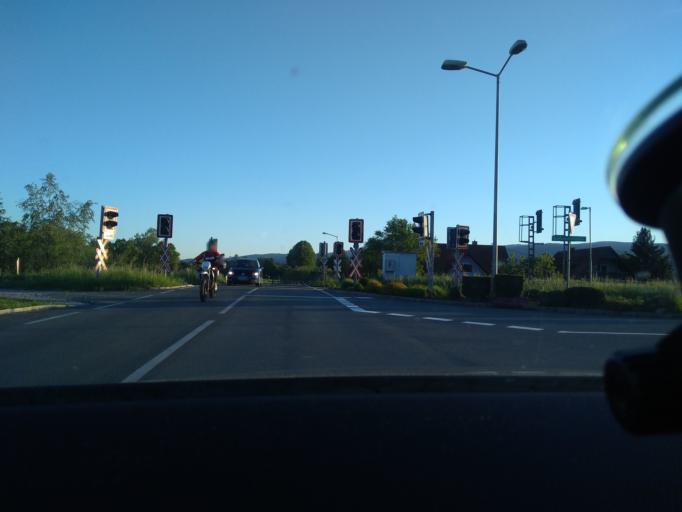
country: AT
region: Styria
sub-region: Politischer Bezirk Voitsberg
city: Mooskirchen
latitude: 46.9959
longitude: 15.2851
